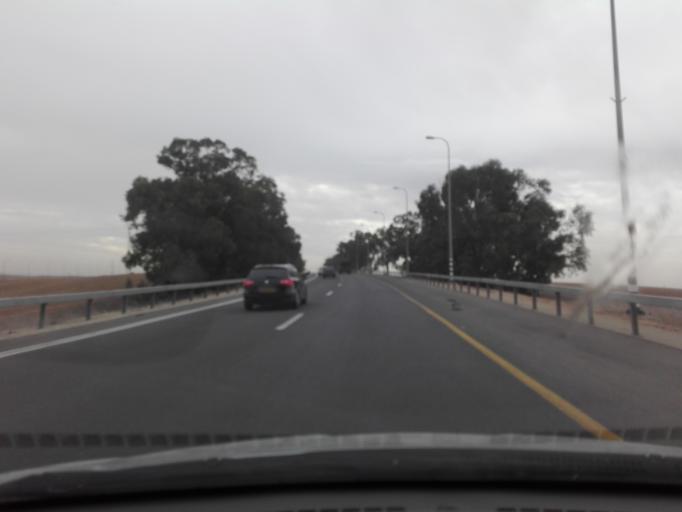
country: IL
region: Southern District
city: Lehavim
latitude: 31.4832
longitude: 34.7757
